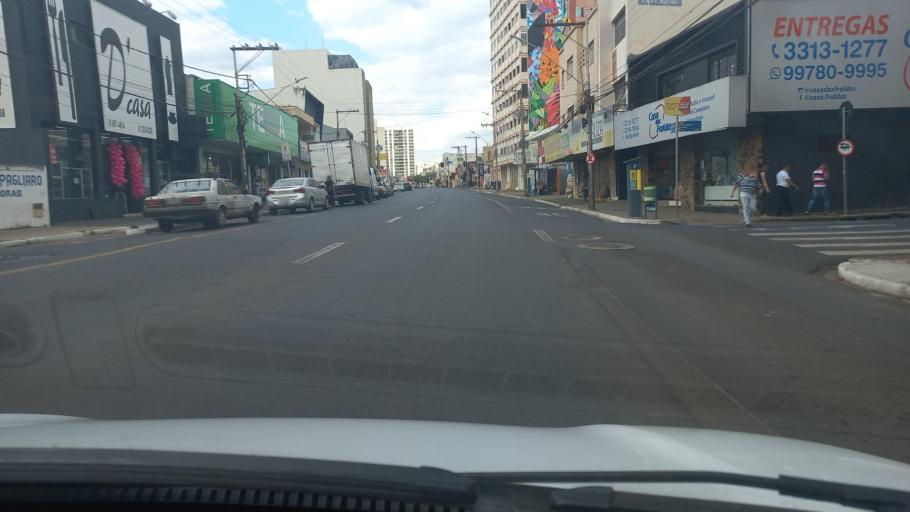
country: BR
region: Minas Gerais
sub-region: Uberaba
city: Uberaba
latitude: -19.7470
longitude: -47.9349
